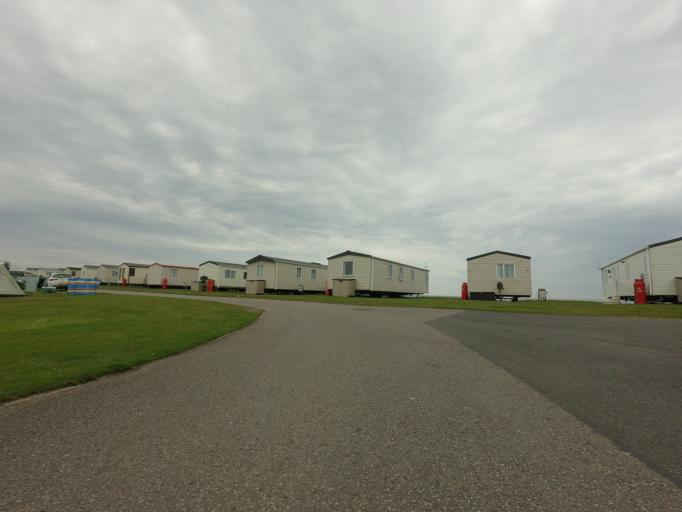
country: GB
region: Scotland
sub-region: Aberdeenshire
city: Banff
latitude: 57.6703
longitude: -2.5535
